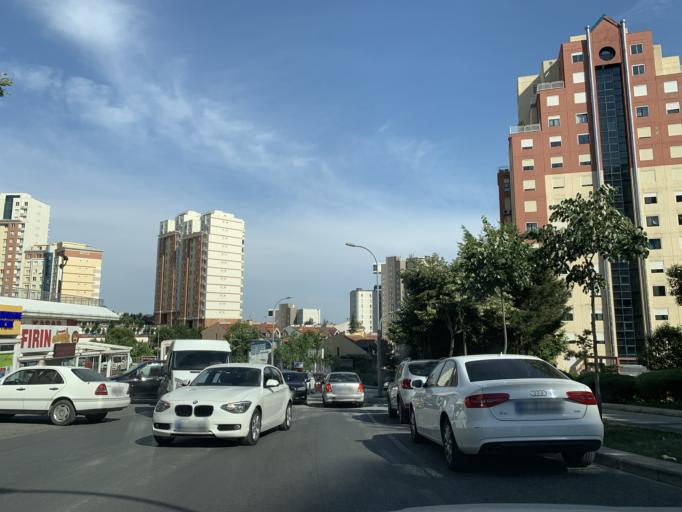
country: TR
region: Istanbul
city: Esenyurt
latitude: 41.0725
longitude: 28.6835
